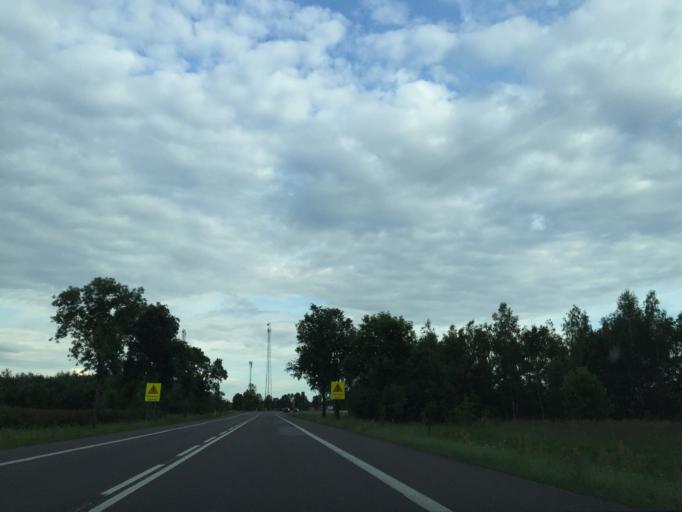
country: PL
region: Lublin Voivodeship
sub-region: Powiat lubartowski
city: Firlej
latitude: 51.5681
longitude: 22.5013
